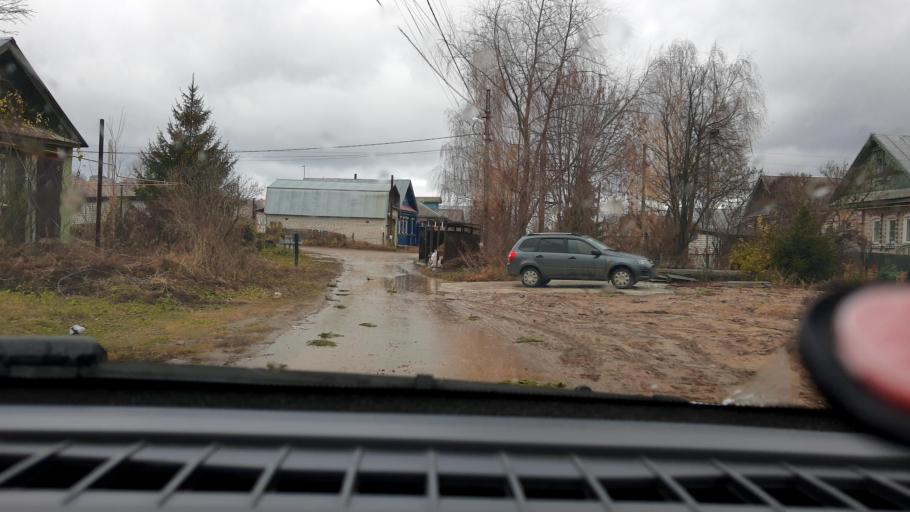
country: RU
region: Nizjnij Novgorod
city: Afonino
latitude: 56.2726
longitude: 44.1069
